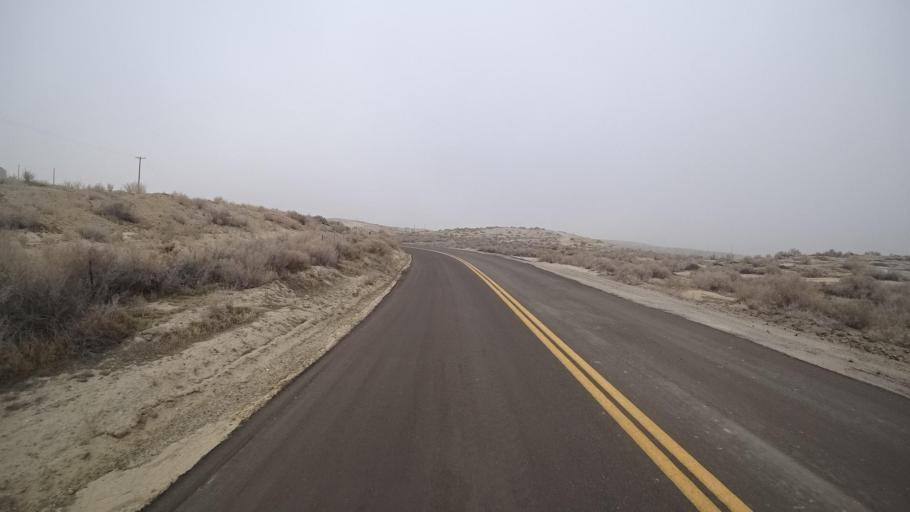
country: US
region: California
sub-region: Kern County
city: Ford City
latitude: 35.1620
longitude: -119.3779
